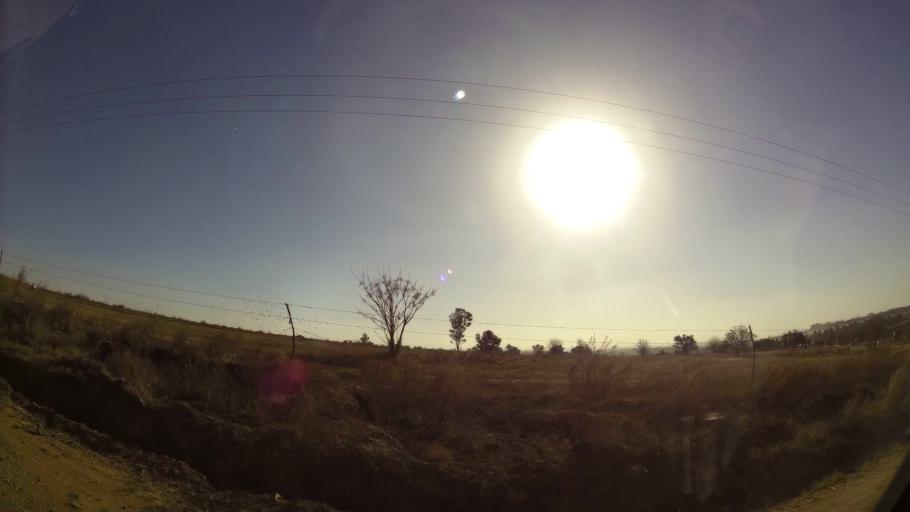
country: ZA
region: Gauteng
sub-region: City of Johannesburg Metropolitan Municipality
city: Diepsloot
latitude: -25.9556
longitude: 27.9590
